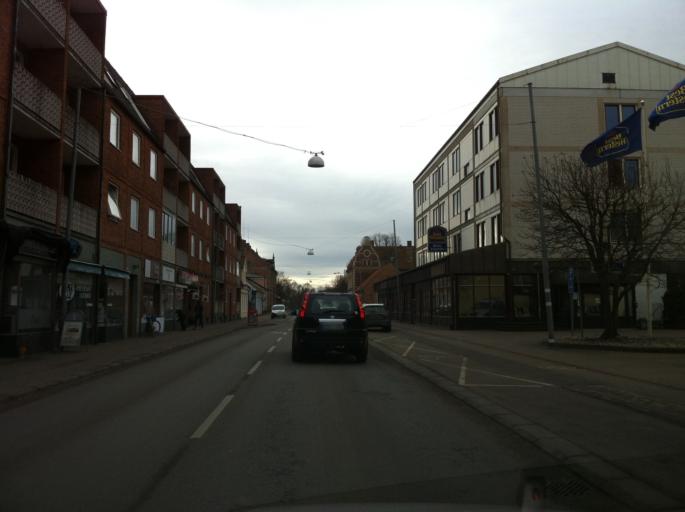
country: SE
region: Skane
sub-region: Angelholms Kommun
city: AEngelholm
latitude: 56.2470
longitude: 12.8669
